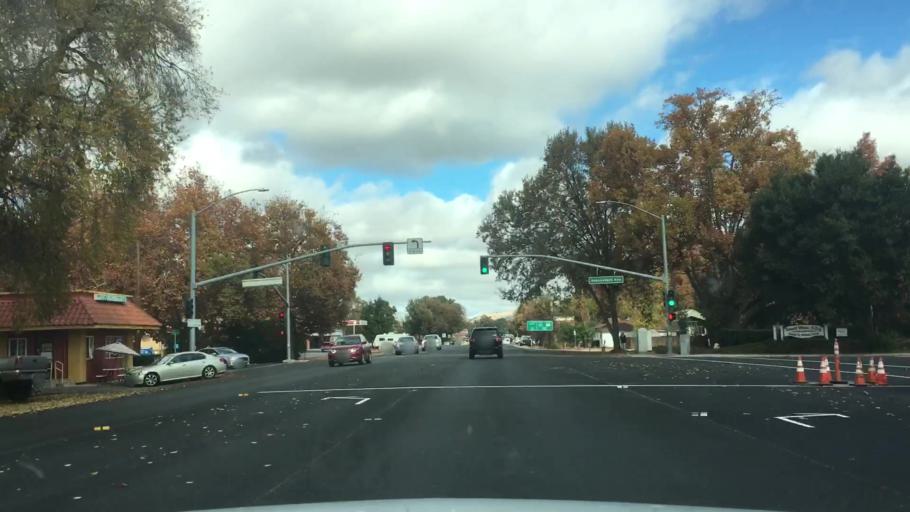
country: US
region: California
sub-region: San Luis Obispo County
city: Atascadero
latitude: 35.4803
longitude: -120.6665
